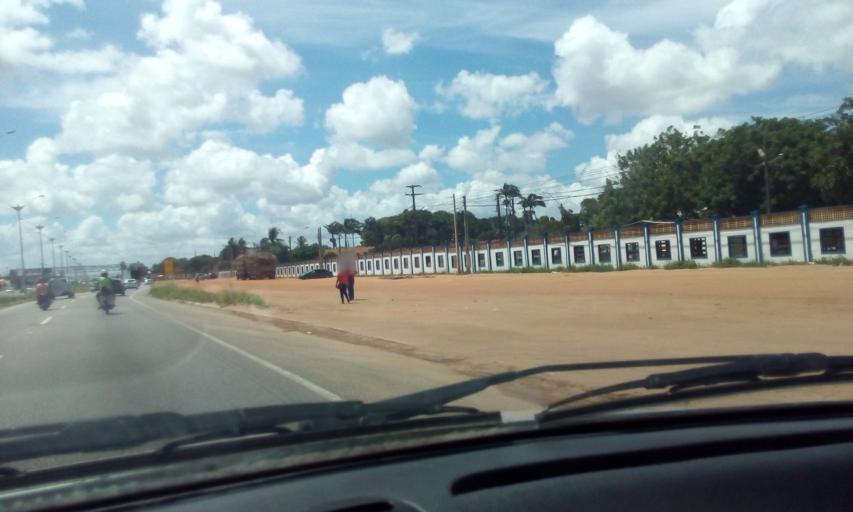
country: BR
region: Rio Grande do Norte
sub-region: Parnamirim
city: Parnamirim
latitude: -5.9027
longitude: -35.2598
